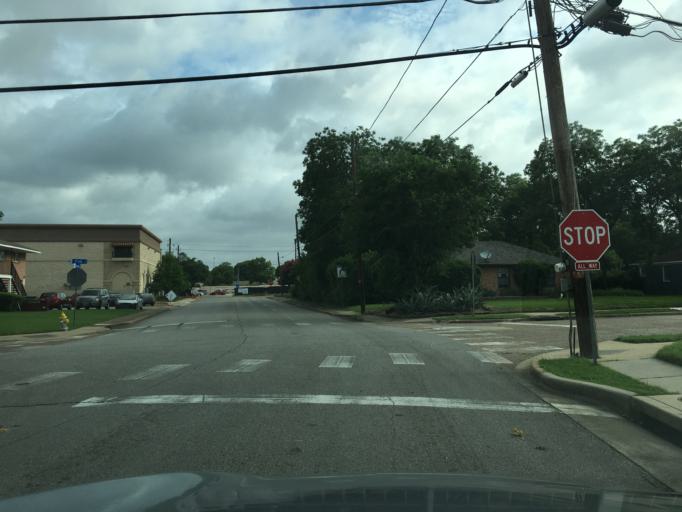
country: US
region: Texas
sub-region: Dallas County
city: Richardson
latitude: 32.9472
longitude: -96.7277
